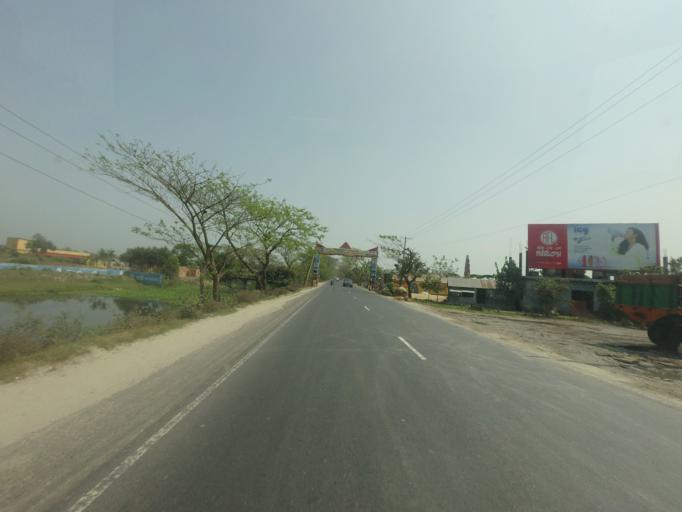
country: BD
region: Dhaka
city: Bhairab Bazar
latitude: 24.0450
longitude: 91.0697
